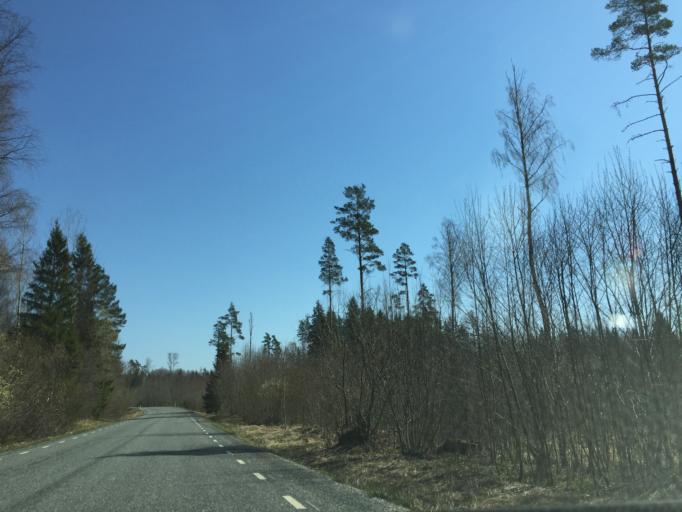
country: EE
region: Tartu
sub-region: Alatskivi vald
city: Kallaste
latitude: 58.5950
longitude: 27.0739
